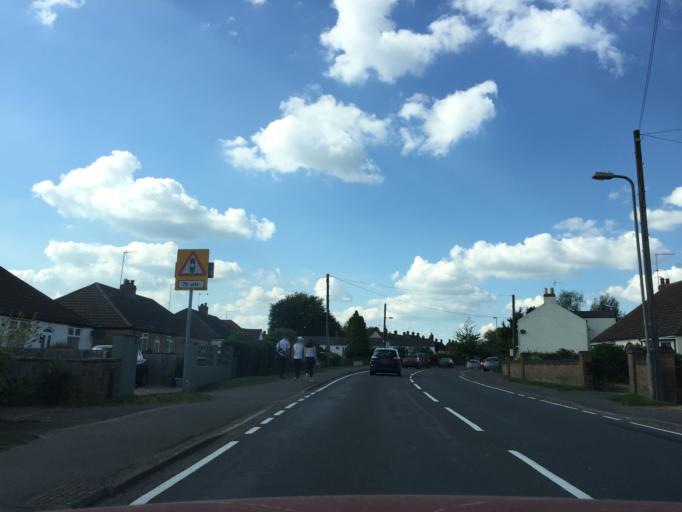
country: GB
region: England
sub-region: Northamptonshire
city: Roade
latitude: 52.1586
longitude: -0.8978
